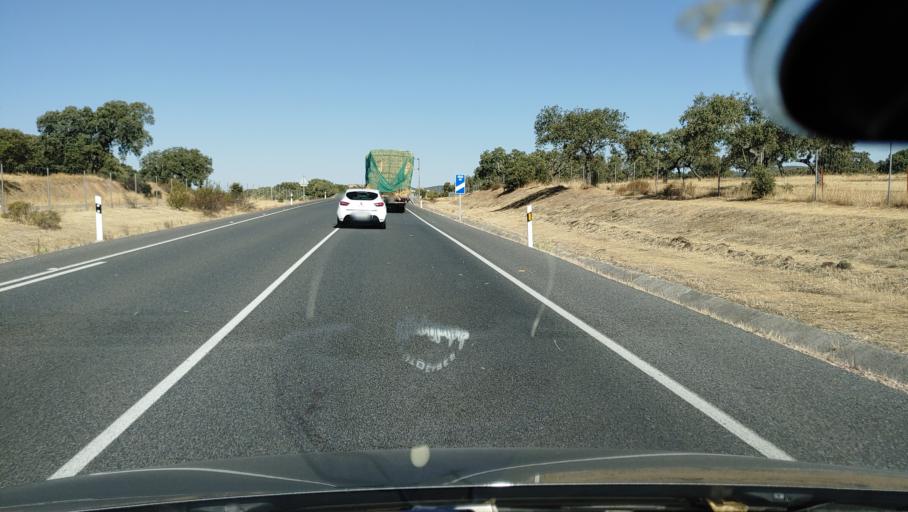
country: ES
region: Andalusia
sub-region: Province of Cordoba
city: Obejo
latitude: 38.0737
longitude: -4.8422
